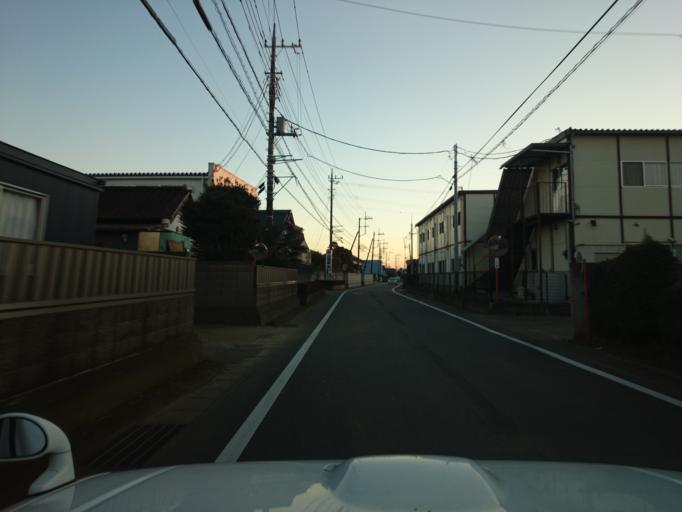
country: JP
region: Ibaraki
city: Ishige
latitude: 36.0885
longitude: 140.0481
